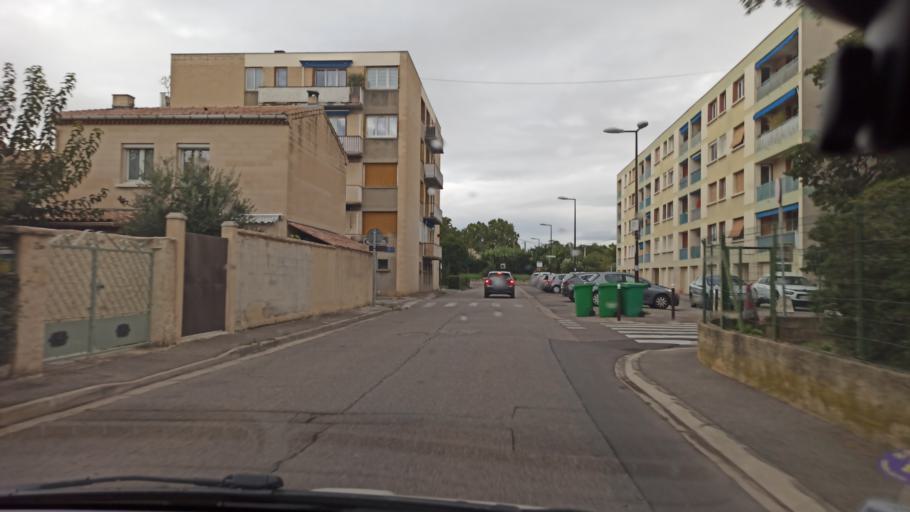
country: FR
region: Provence-Alpes-Cote d'Azur
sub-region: Departement du Vaucluse
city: Montfavet
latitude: 43.9410
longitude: 4.8761
